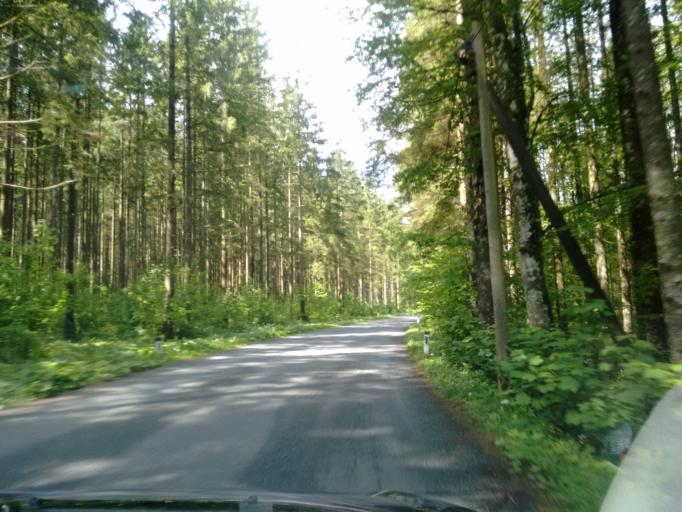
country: AT
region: Upper Austria
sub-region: Politischer Bezirk Gmunden
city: Ebensee
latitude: 47.8361
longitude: 13.6982
